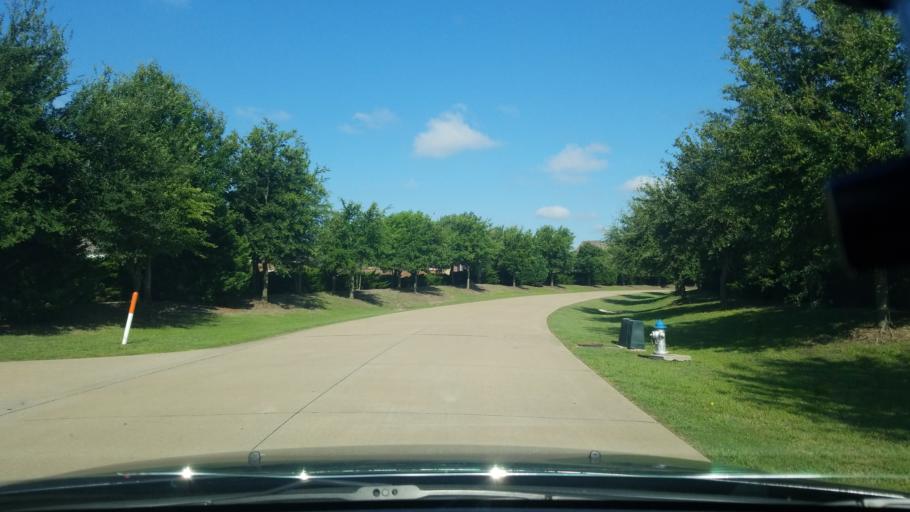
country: US
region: Texas
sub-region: Dallas County
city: Sunnyvale
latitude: 32.8056
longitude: -96.5801
